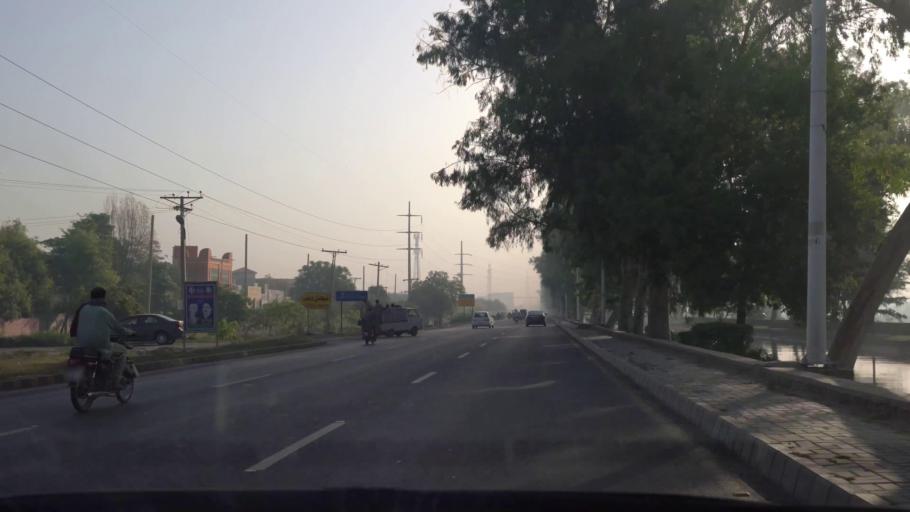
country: PK
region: Punjab
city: Faisalabad
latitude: 31.4561
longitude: 73.1632
